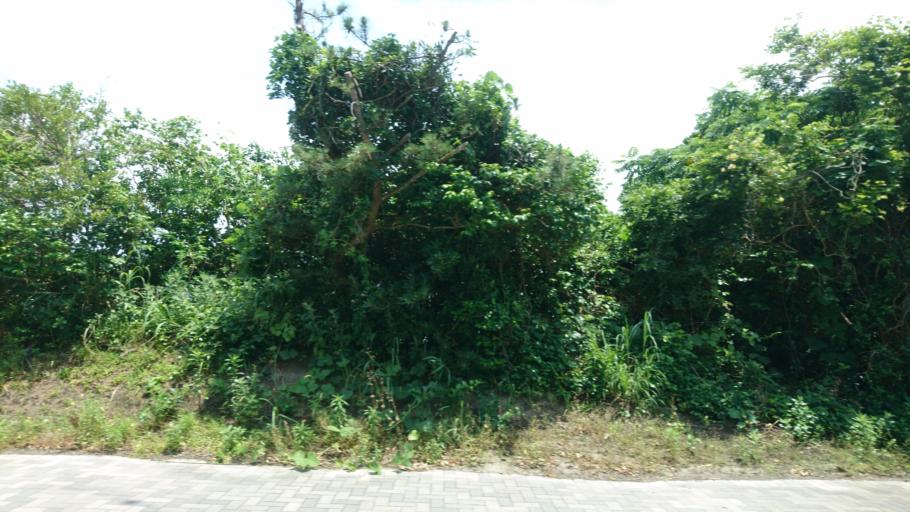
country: JP
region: Shizuoka
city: Shimoda
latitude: 34.3723
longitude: 139.2690
